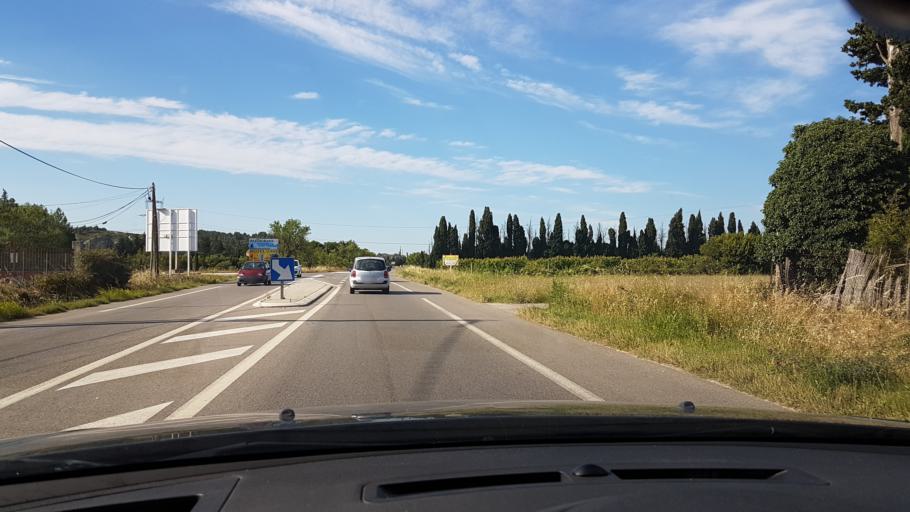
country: FR
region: Provence-Alpes-Cote d'Azur
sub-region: Departement des Bouches-du-Rhone
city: Graveson
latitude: 43.8596
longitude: 4.7688
